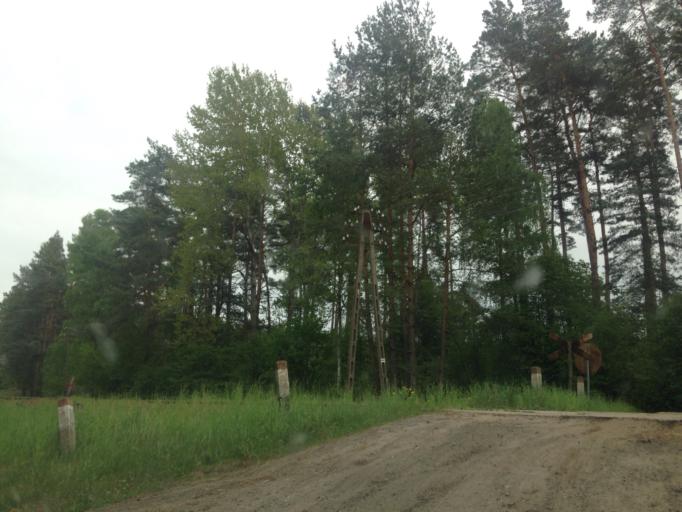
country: PL
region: Kujawsko-Pomorskie
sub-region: Powiat brodnicki
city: Bartniczka
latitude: 53.2679
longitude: 19.5499
